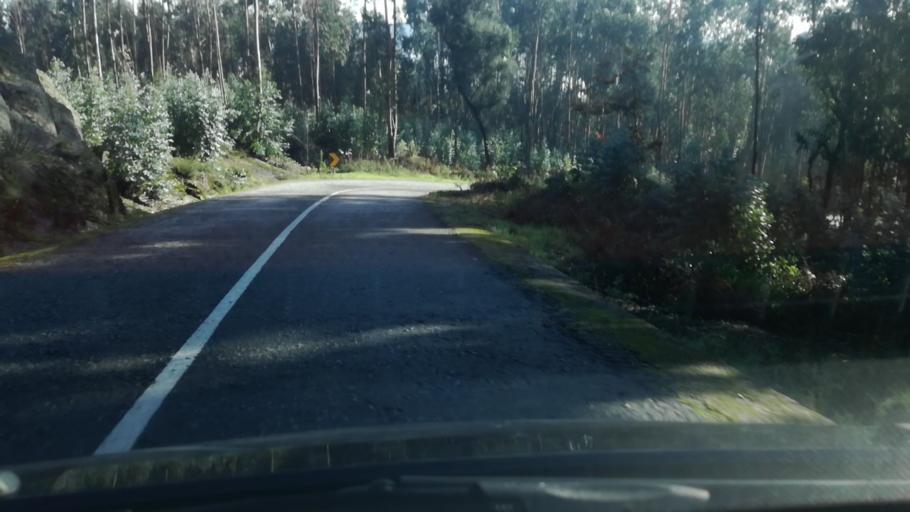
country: PT
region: Braga
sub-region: Guimaraes
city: Ponte
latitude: 41.5317
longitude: -8.3471
